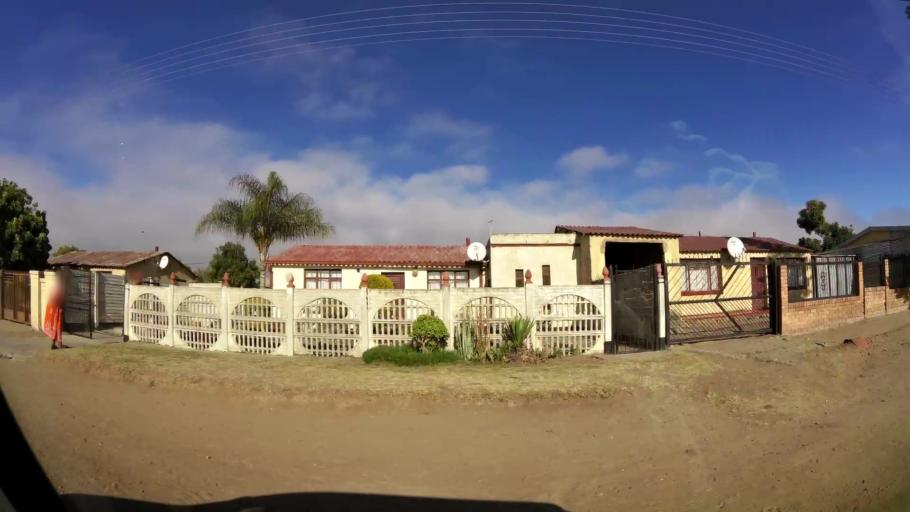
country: ZA
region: Limpopo
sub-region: Capricorn District Municipality
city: Polokwane
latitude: -23.8479
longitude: 29.3892
